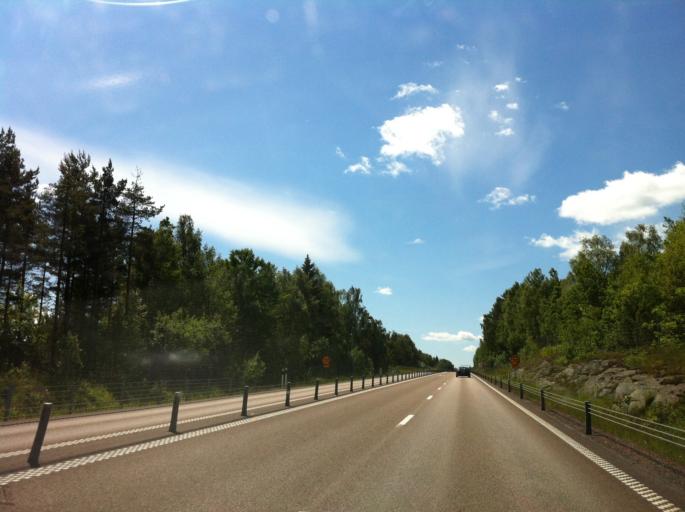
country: SE
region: Vaestra Goetaland
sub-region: Melleruds Kommun
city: Mellerud
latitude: 58.7922
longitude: 12.5178
